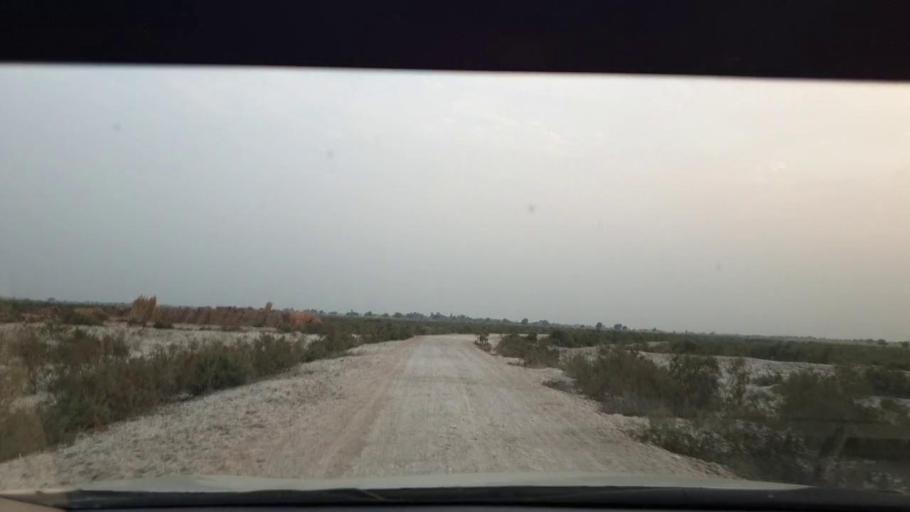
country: PK
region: Sindh
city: Berani
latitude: 25.8778
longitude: 68.7621
